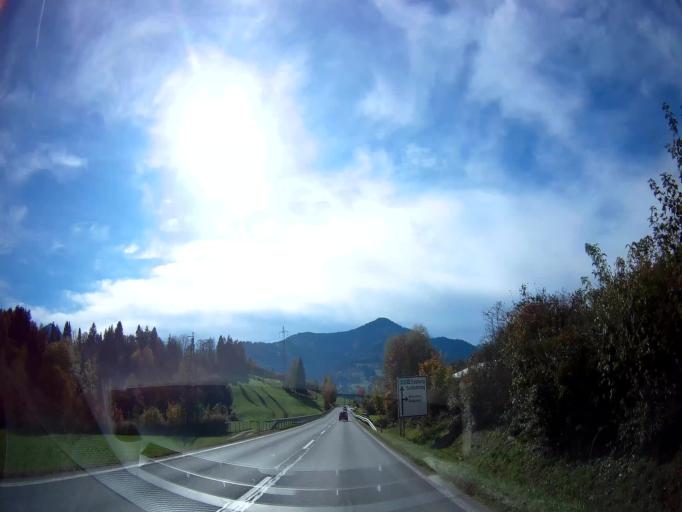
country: AT
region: Styria
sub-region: Politischer Bezirk Liezen
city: Grobming
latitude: 47.4497
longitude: 13.9124
